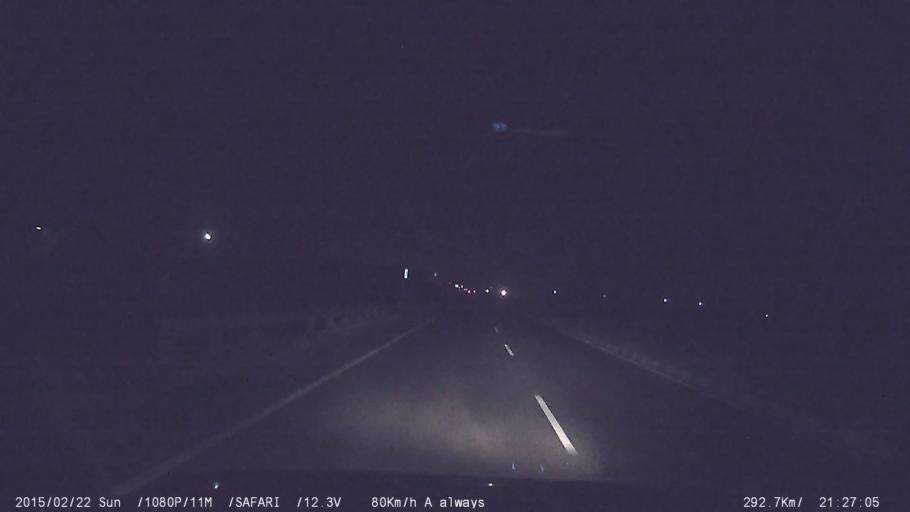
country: IN
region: Tamil Nadu
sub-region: Karur
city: Karur
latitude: 10.9120
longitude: 78.0407
